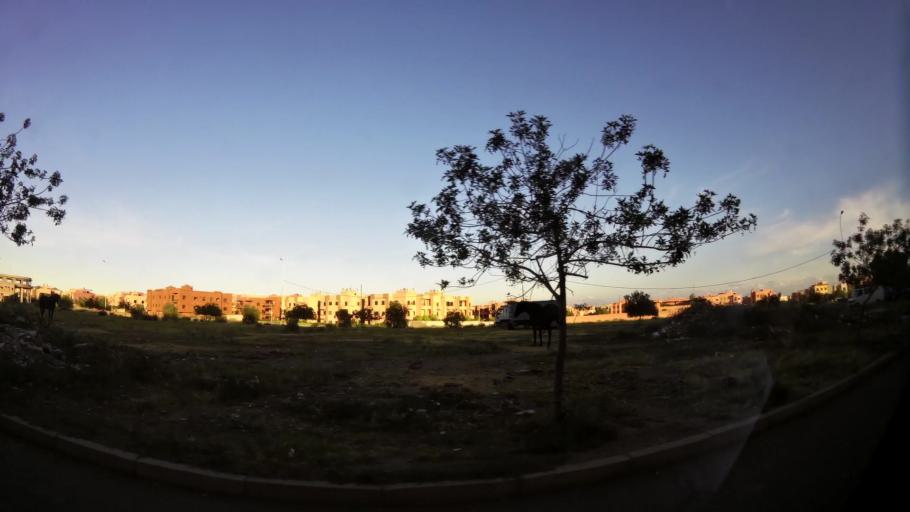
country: MA
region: Marrakech-Tensift-Al Haouz
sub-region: Marrakech
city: Marrakesh
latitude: 31.7491
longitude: -8.1116
